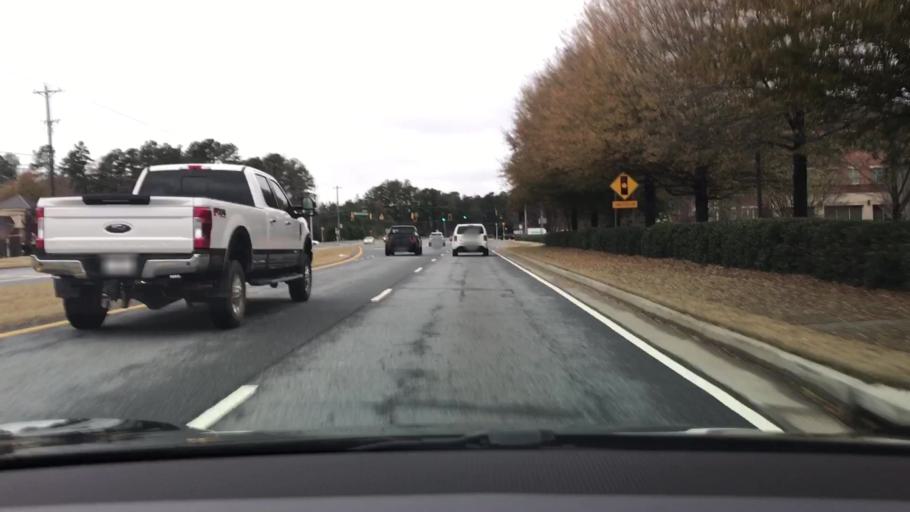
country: US
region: Georgia
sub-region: Fulton County
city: Johns Creek
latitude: 34.0615
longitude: -84.1569
